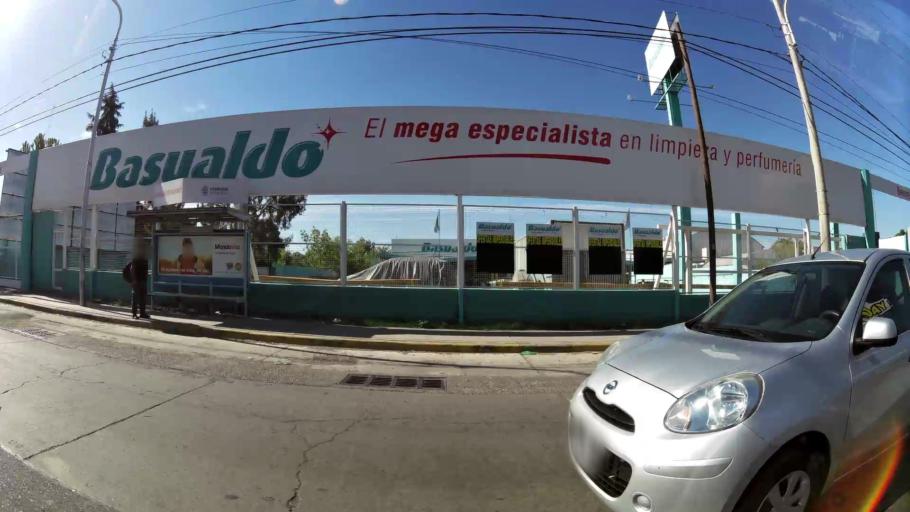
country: AR
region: Mendoza
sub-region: Departamento de Godoy Cruz
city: Godoy Cruz
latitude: -32.9283
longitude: -68.8143
